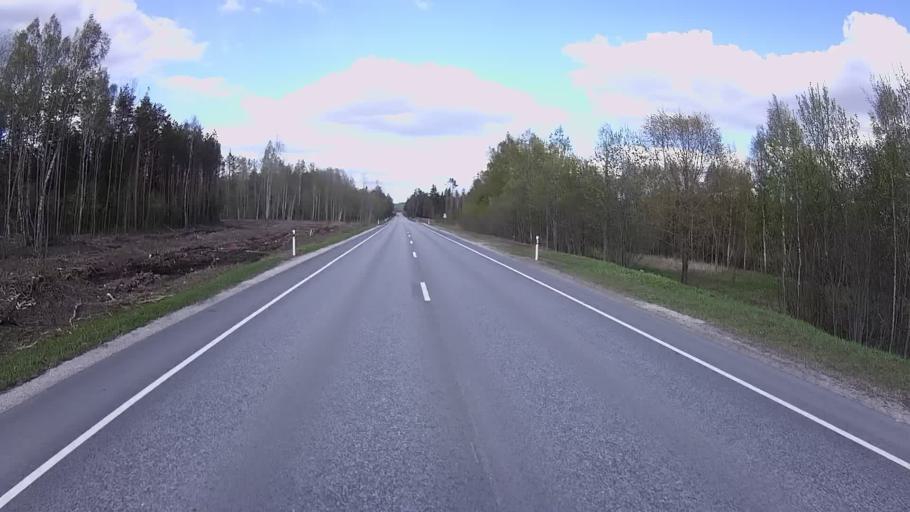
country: EE
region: Jogevamaa
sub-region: Jogeva linn
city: Jogeva
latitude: 58.7646
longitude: 26.4353
